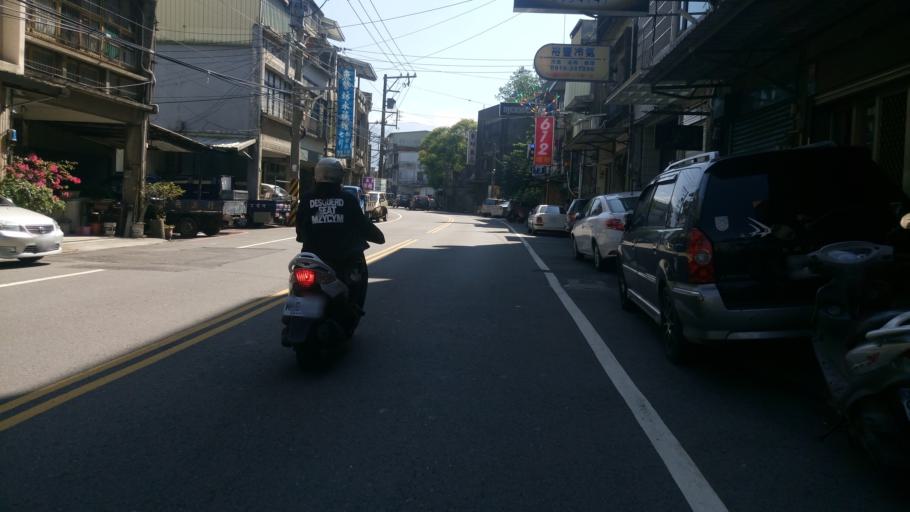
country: TW
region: Taiwan
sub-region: Hsinchu
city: Zhubei
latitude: 24.7311
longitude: 121.0902
